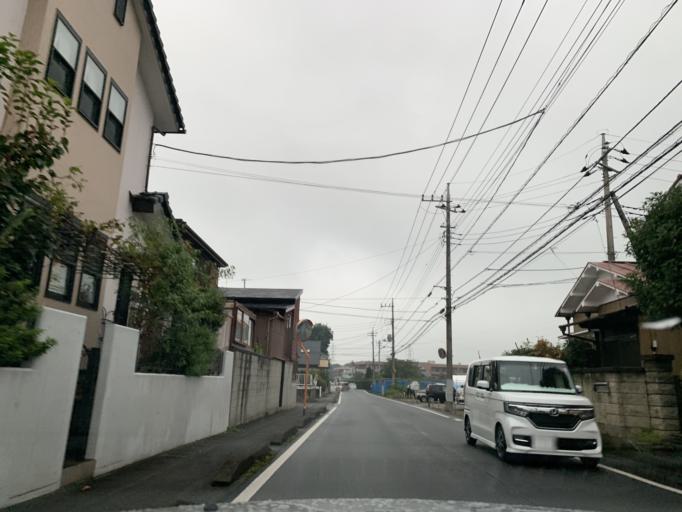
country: JP
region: Chiba
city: Nagareyama
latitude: 35.9064
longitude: 139.9186
